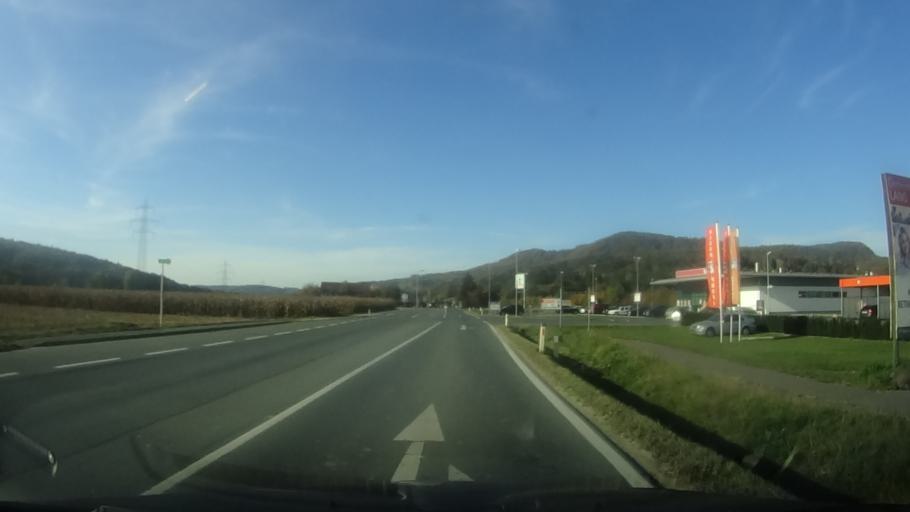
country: AT
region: Styria
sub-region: Politischer Bezirk Leibnitz
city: Lang
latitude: 46.8509
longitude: 15.5139
